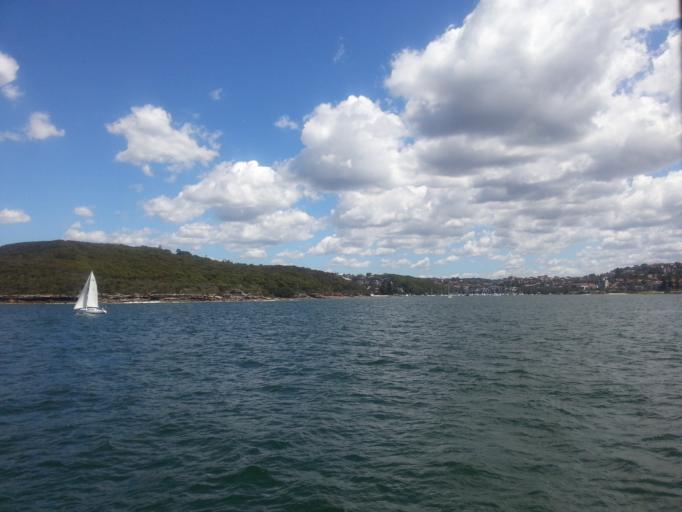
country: AU
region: New South Wales
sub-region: Manly Vale
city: Manly
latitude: -33.8102
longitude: 151.2800
